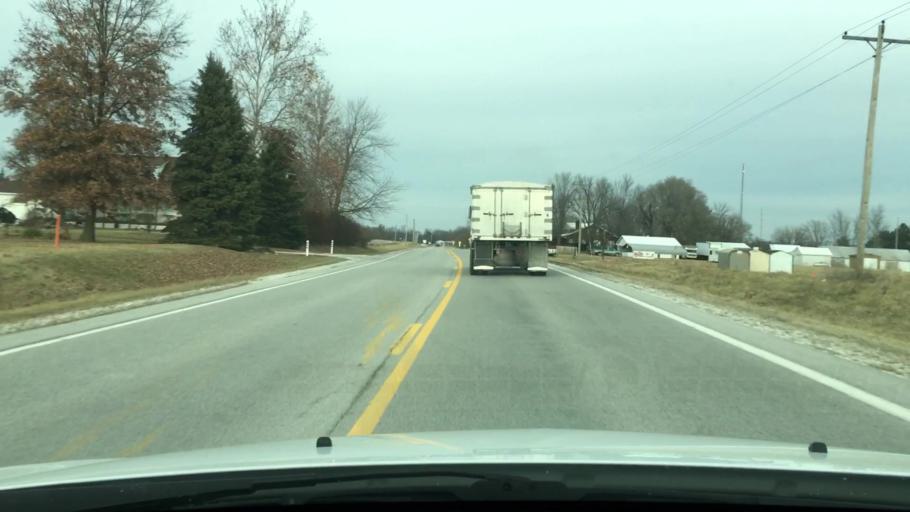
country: US
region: Illinois
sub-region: Pike County
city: Pittsfield
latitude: 39.6467
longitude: -90.7843
